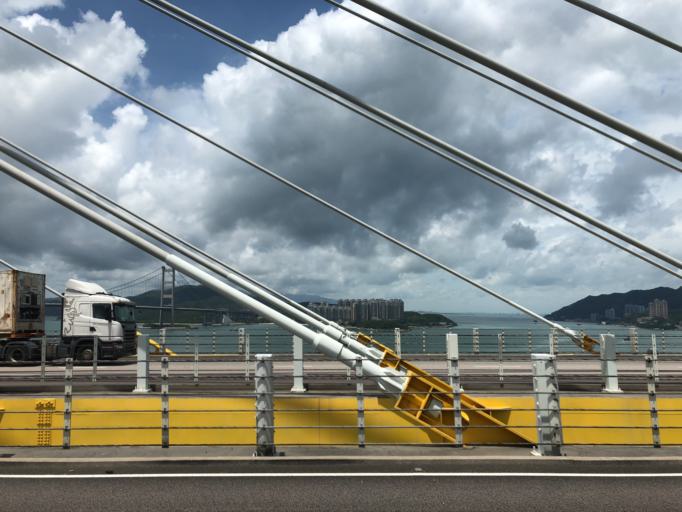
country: HK
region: Tsuen Wan
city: Tsuen Wan
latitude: 22.3616
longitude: 114.0812
